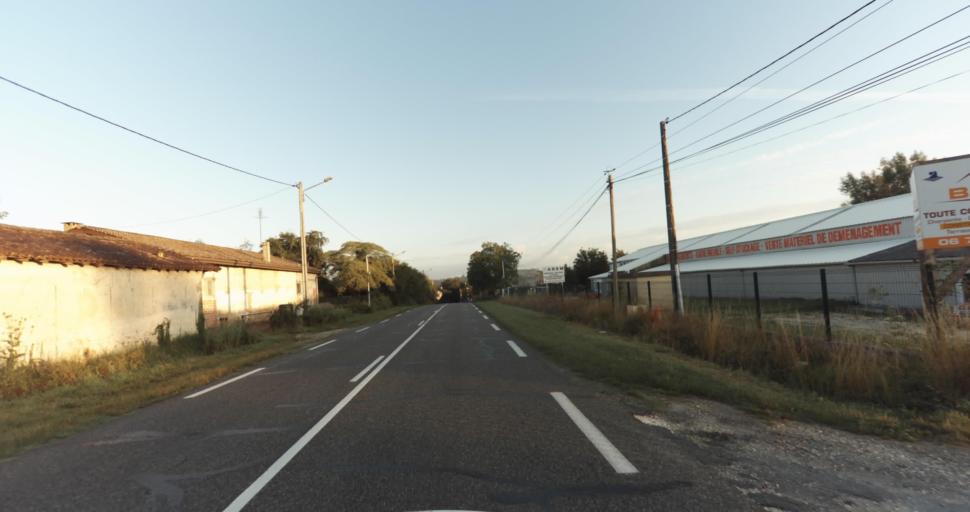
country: FR
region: Aquitaine
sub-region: Departement de la Gironde
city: Bazas
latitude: 44.4303
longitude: -0.1963
